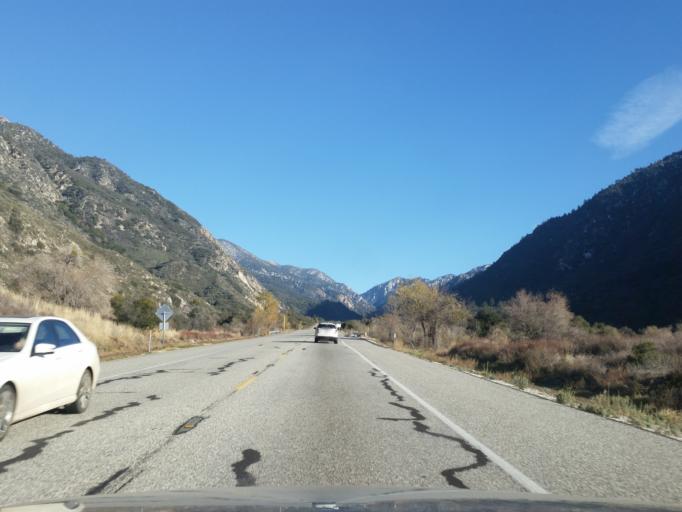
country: US
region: California
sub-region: San Bernardino County
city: Yucaipa
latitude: 34.0988
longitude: -116.9805
